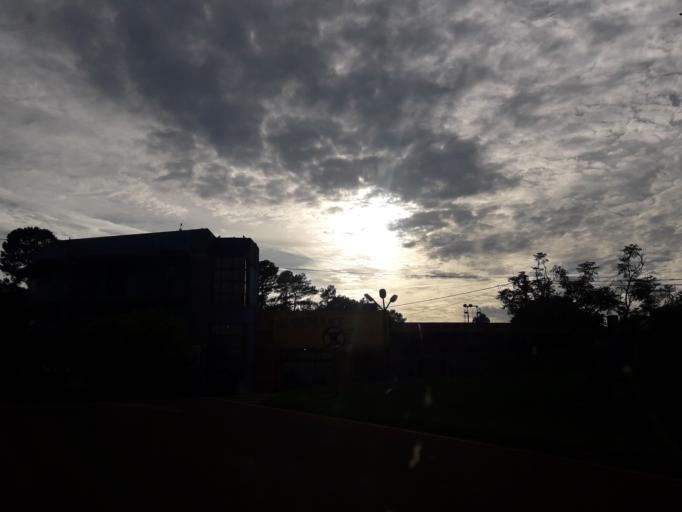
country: AR
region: Misiones
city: Dos de Mayo
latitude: -26.9888
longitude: -54.4784
